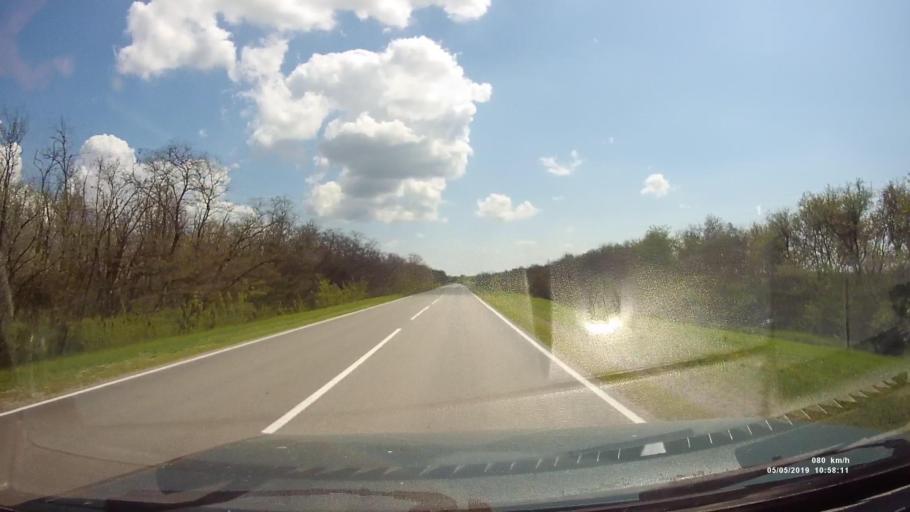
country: RU
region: Rostov
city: Ust'-Donetskiy
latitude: 47.6703
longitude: 40.8484
